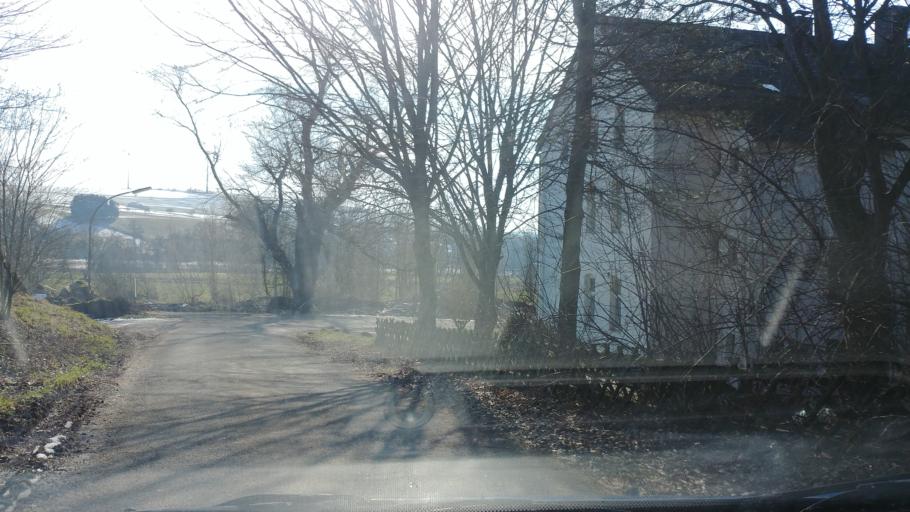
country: DE
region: Lower Saxony
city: Uslar
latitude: 51.6546
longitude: 9.6690
